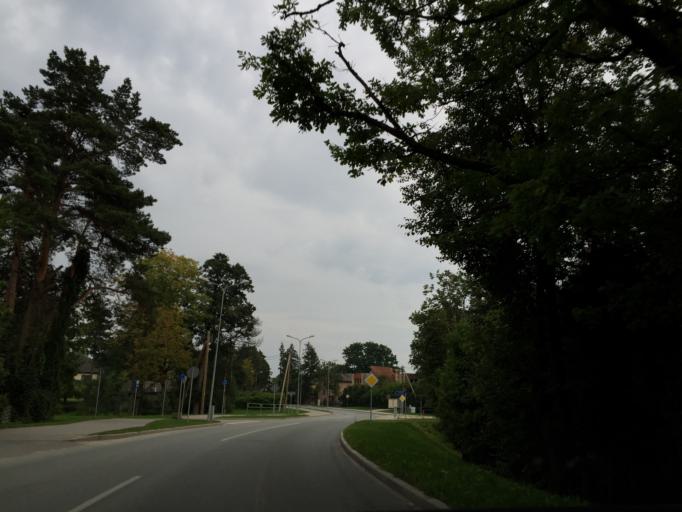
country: LV
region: Ogre
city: Ogre
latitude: 56.8143
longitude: 24.6307
